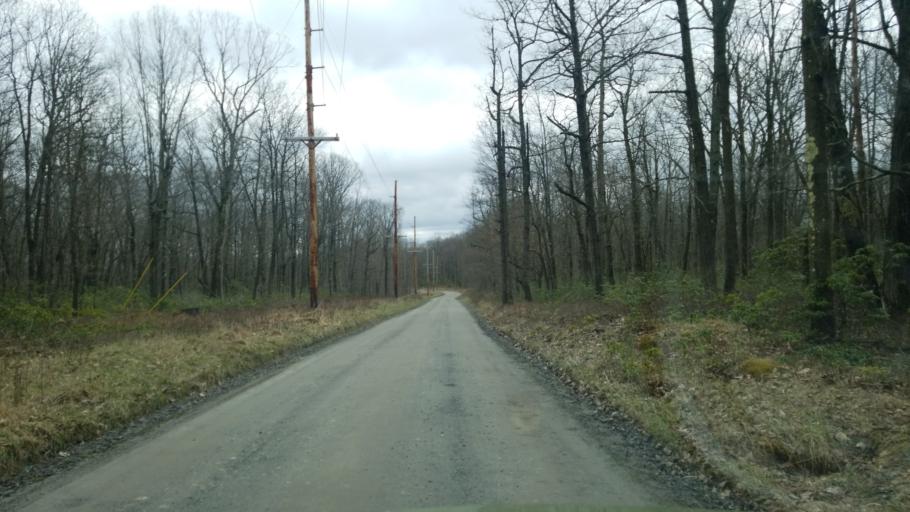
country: US
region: Pennsylvania
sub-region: Clearfield County
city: Shiloh
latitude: 41.1726
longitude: -78.2973
